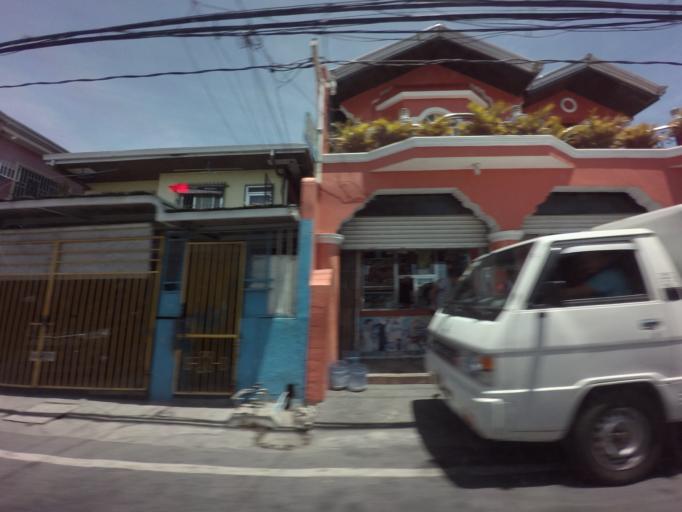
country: PH
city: Sambayanihan People's Village
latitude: 14.4609
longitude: 121.0543
